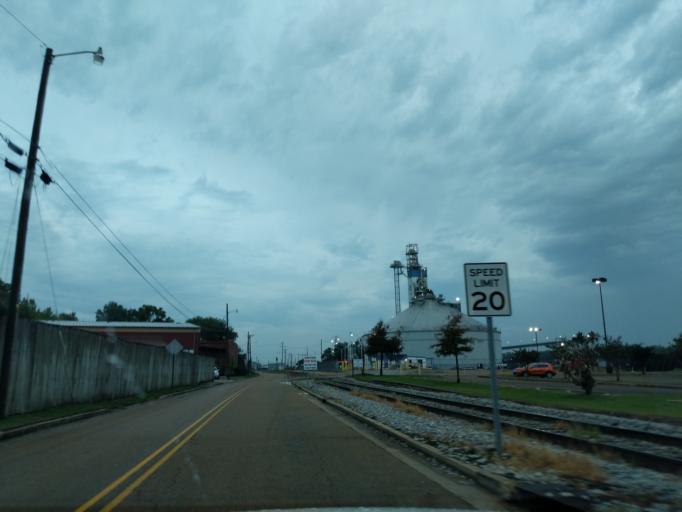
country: US
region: Mississippi
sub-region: Warren County
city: Vicksburg
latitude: 32.3483
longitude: -90.8852
